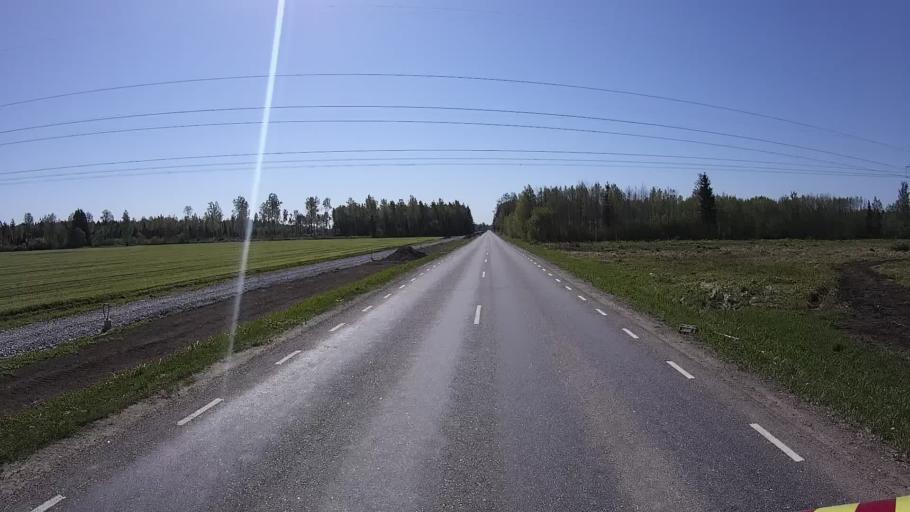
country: EE
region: Paernumaa
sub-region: Tootsi vald
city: Tootsi
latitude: 58.5014
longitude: 24.7992
